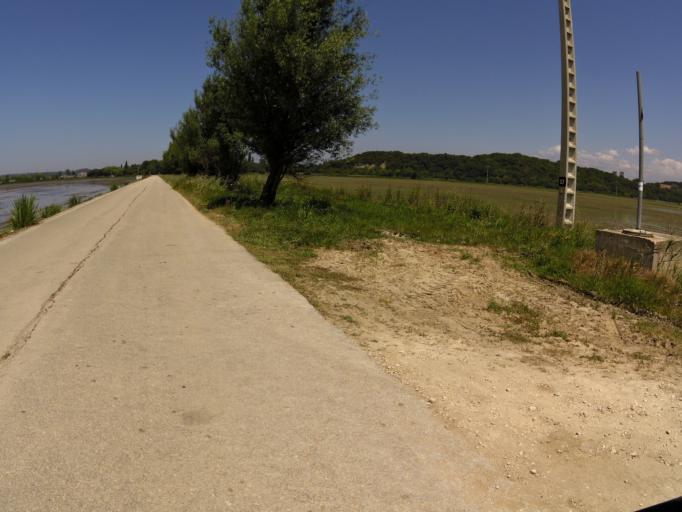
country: PT
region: Coimbra
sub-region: Montemor-O-Velho
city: Montemor-o-Velho
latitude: 40.1651
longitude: -8.7180
